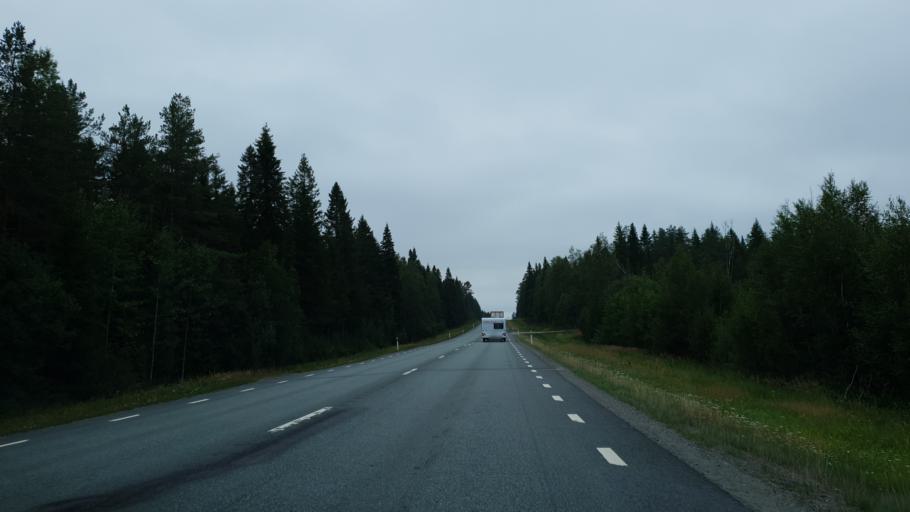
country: SE
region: Vaesterbotten
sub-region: Skelleftea Kommun
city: Burea
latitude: 64.3555
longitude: 21.2948
